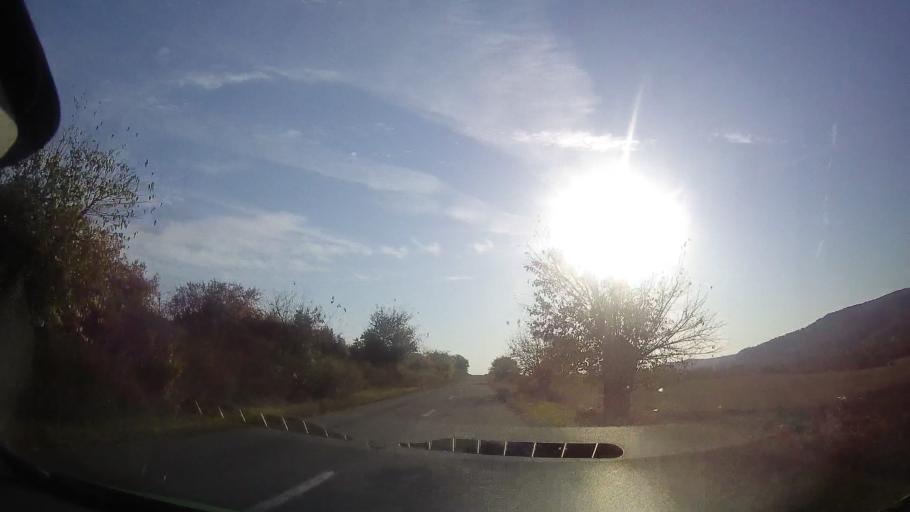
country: RO
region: Timis
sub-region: Comuna Bogda
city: Bogda
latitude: 45.9816
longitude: 21.5614
